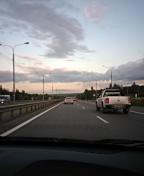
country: RU
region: Moskovskaya
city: Zhukovskiy
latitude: 55.5377
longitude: 38.0935
